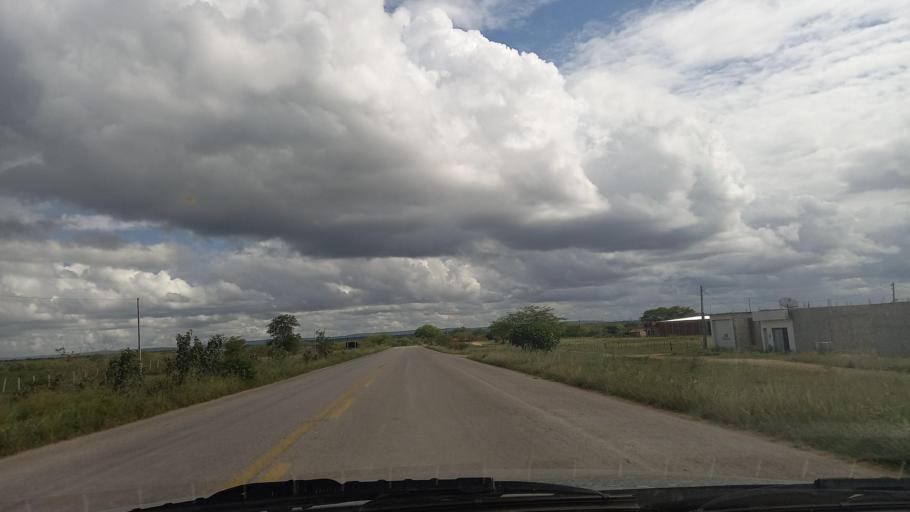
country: BR
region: Pernambuco
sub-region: Cachoeirinha
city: Cachoeirinha
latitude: -8.4996
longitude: -36.2442
